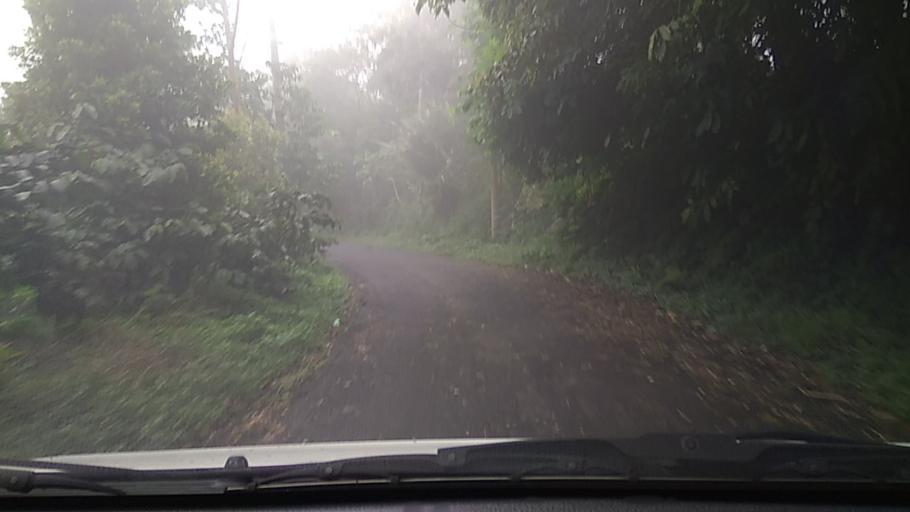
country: ID
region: Bali
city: Banjar Ambengan
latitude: -8.2017
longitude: 115.1757
